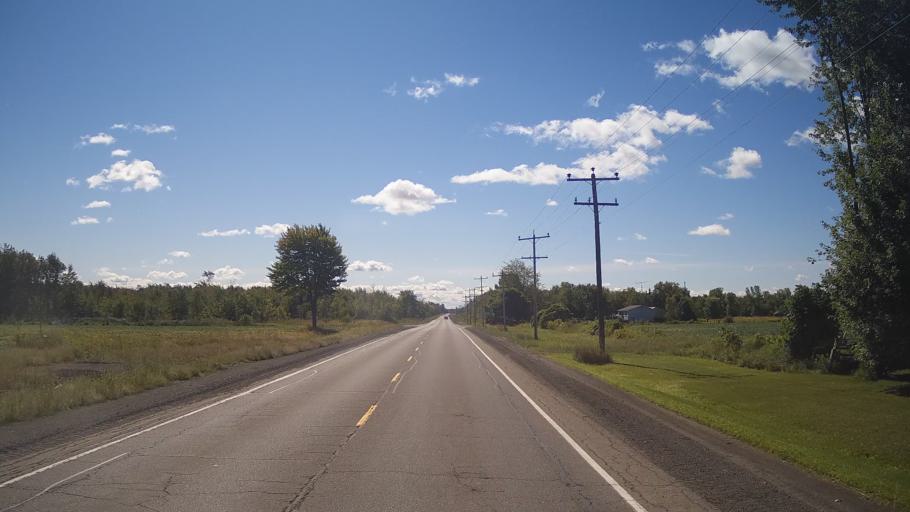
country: US
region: New York
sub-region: St. Lawrence County
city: Norfolk
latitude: 44.9537
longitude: -75.2266
